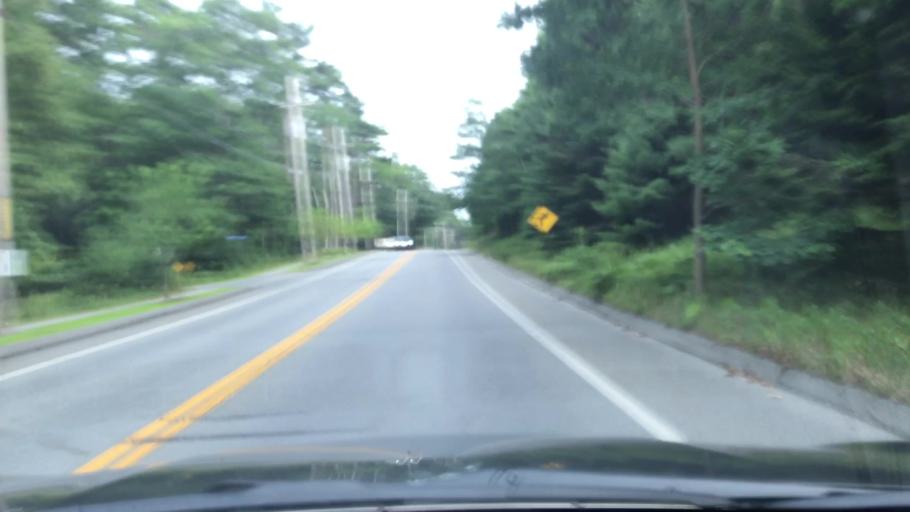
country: US
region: Maine
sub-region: Hancock County
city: Bar Harbor
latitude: 44.3736
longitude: -68.1976
